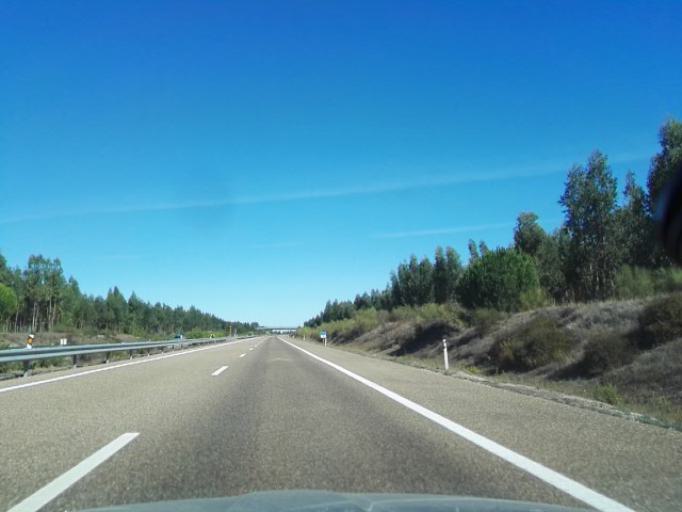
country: PT
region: Evora
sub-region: Vendas Novas
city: Vendas Novas
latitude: 38.6335
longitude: -8.6618
